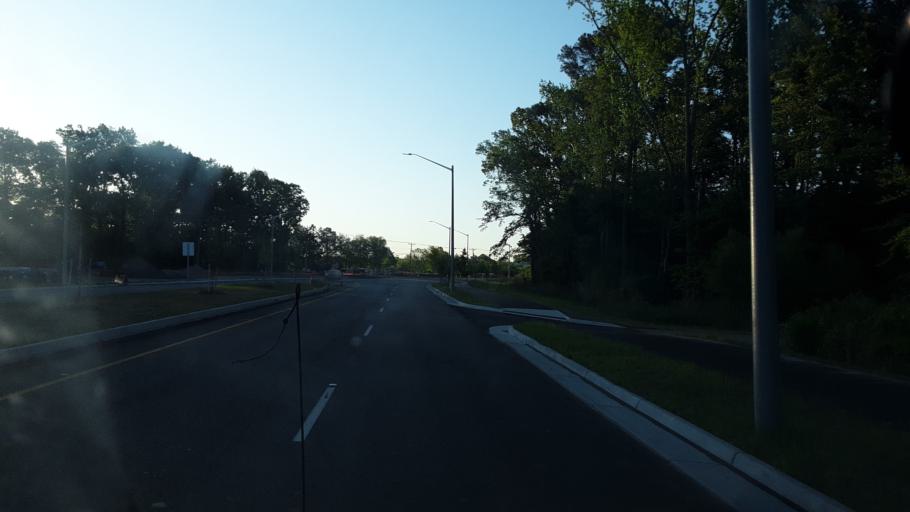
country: US
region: Virginia
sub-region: City of Virginia Beach
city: Virginia Beach
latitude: 36.7584
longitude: -76.0151
